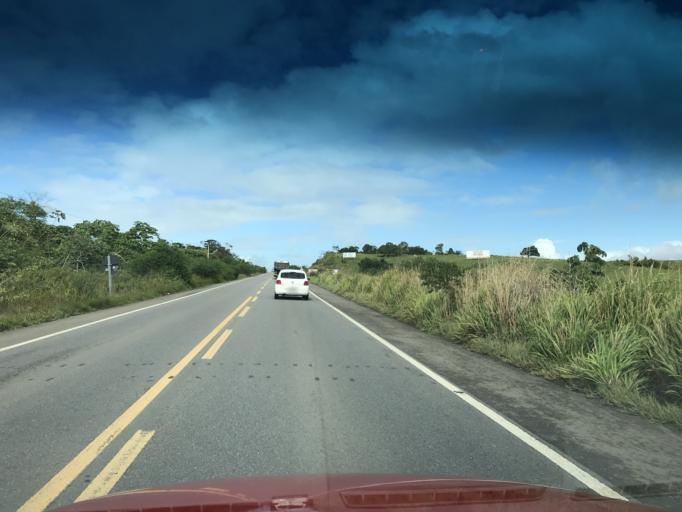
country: BR
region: Bahia
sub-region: Conceicao Do Almeida
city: Muritiba
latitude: -12.9088
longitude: -39.2398
